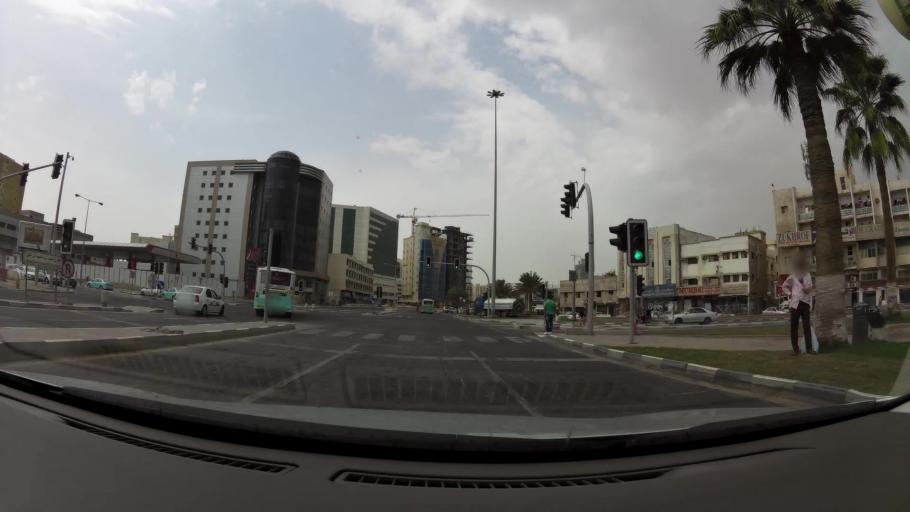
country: QA
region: Baladiyat ad Dawhah
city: Doha
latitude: 25.2797
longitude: 51.5288
